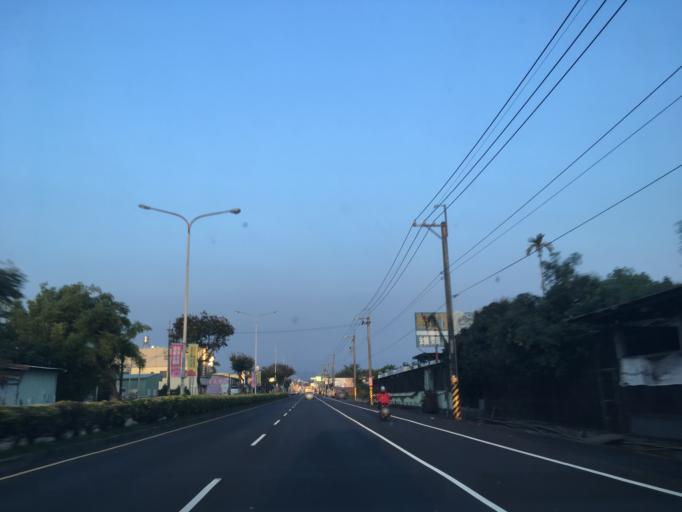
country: TW
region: Taiwan
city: Zhongxing New Village
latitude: 23.9879
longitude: 120.6738
